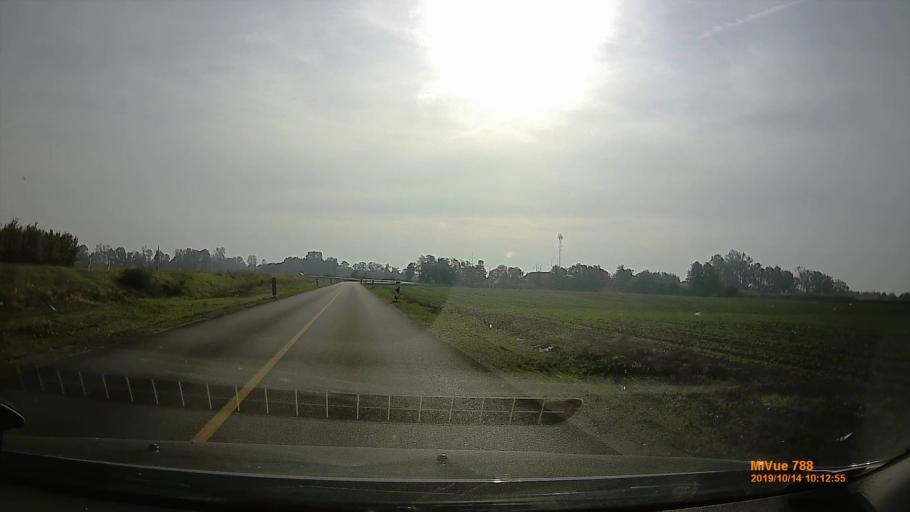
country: HU
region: Pest
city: Tortel
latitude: 47.1888
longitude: 19.9224
